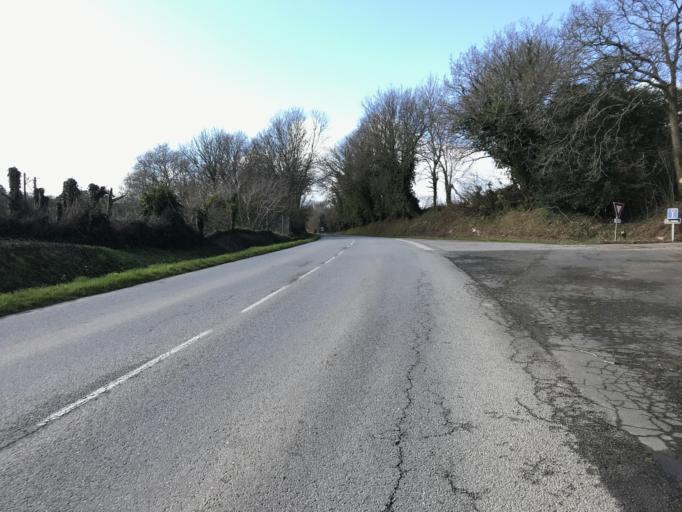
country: FR
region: Brittany
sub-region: Departement du Finistere
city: Loperhet
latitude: 48.3813
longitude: -4.3311
